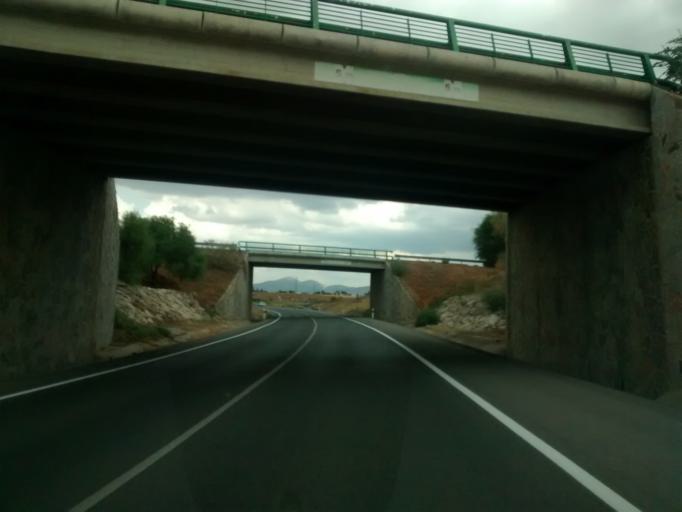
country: ES
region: Andalusia
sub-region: Provincia de Cadiz
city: Villamartin
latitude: 36.8527
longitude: -5.6329
